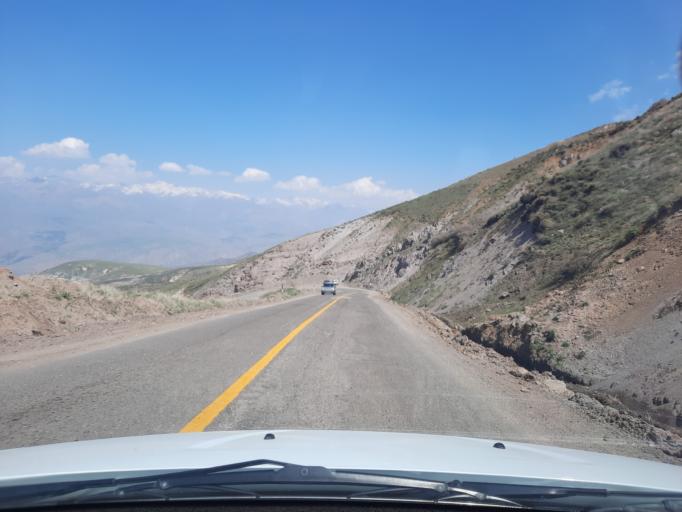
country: IR
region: Qazvin
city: Qazvin
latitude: 36.3954
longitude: 50.2152
